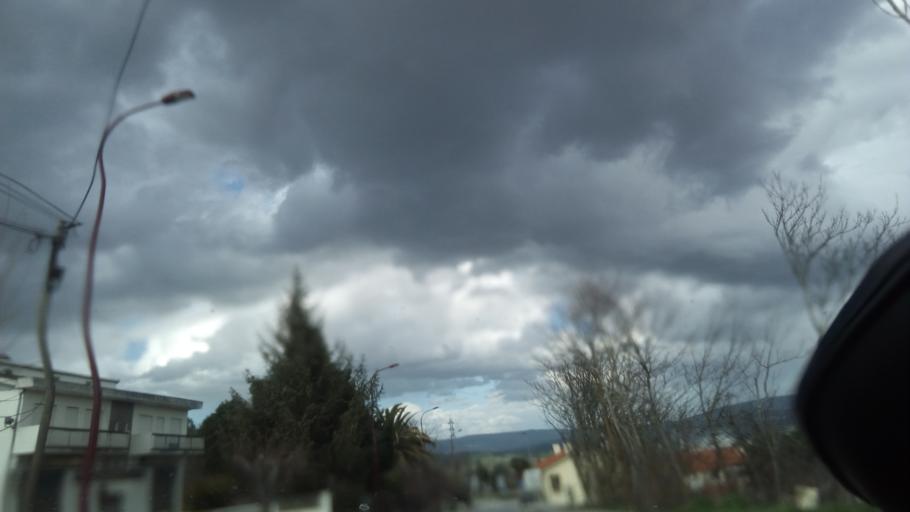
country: PT
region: Guarda
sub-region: Celorico da Beira
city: Celorico da Beira
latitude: 40.6440
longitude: -7.3862
